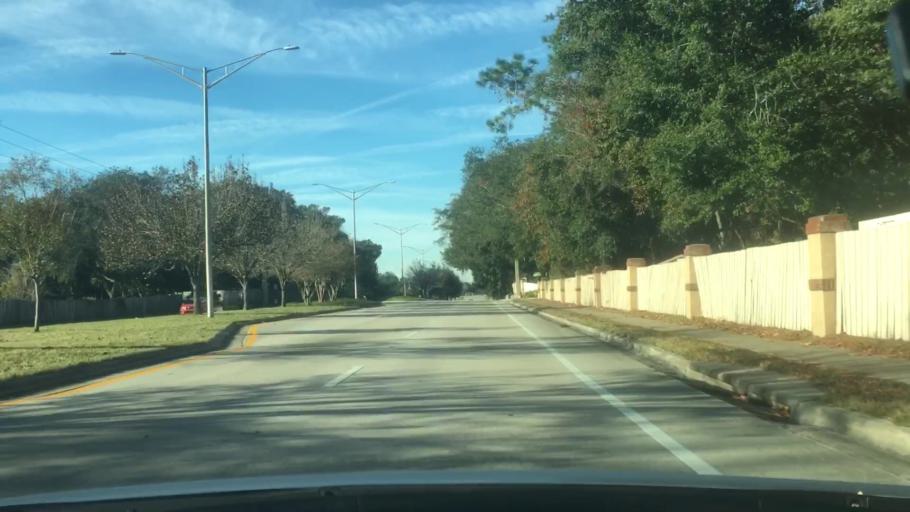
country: US
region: Florida
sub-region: Duval County
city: Atlantic Beach
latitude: 30.3518
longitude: -81.5140
